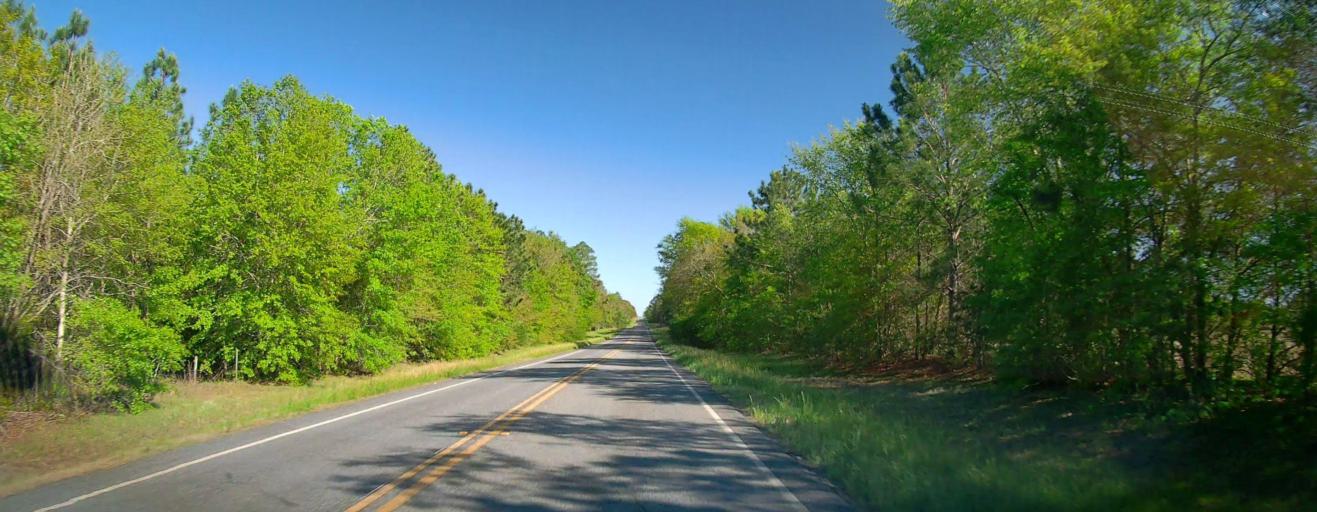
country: US
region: Georgia
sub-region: Wilcox County
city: Rochelle
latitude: 32.0092
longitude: -83.4902
